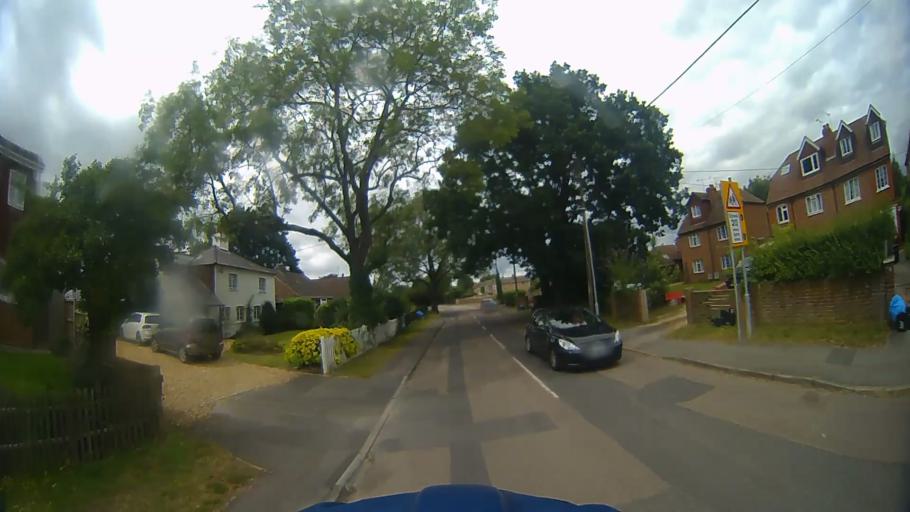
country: GB
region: England
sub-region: Wokingham
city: Winnersh
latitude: 51.4336
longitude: -0.8717
